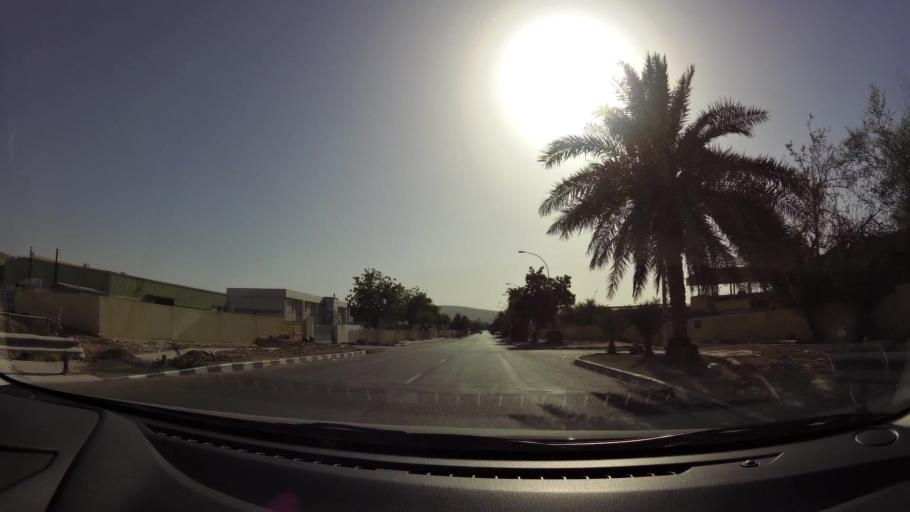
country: OM
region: Muhafazat Masqat
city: As Sib al Jadidah
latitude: 23.5543
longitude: 58.2111
